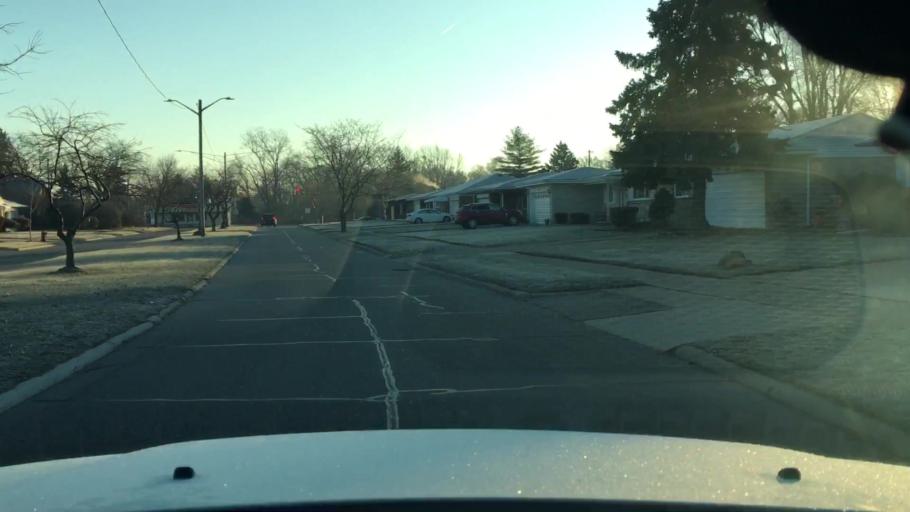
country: US
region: Michigan
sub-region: Oakland County
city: Madison Heights
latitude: 42.4834
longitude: -83.0685
